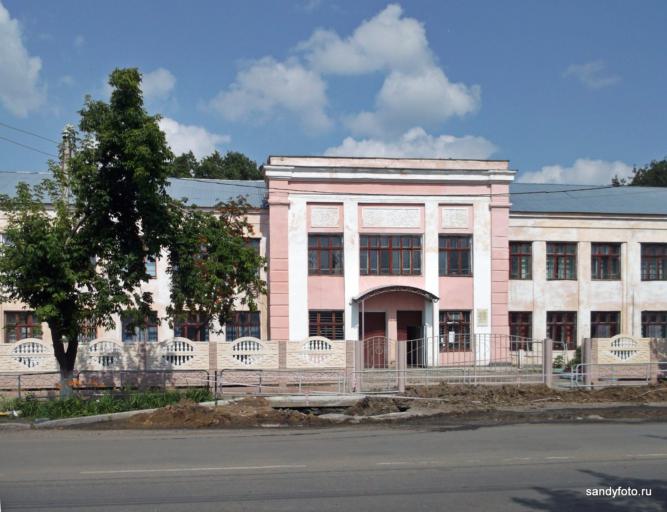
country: RU
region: Chelyabinsk
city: Troitsk
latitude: 54.1108
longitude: 61.5678
